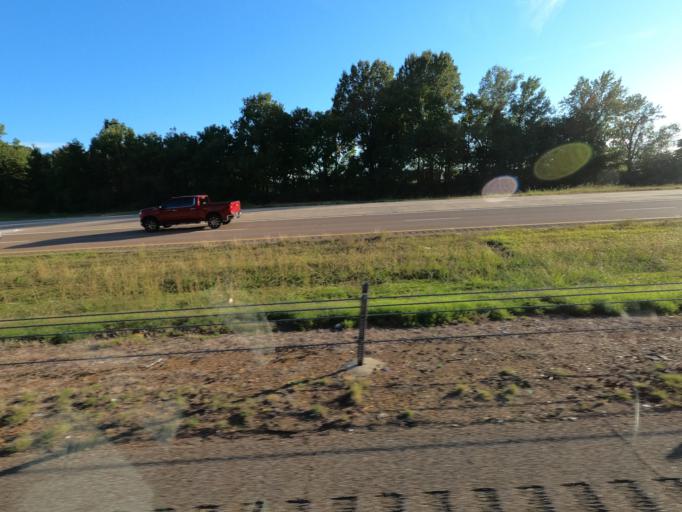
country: US
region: Tennessee
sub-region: Shelby County
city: Millington
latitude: 35.3081
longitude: -89.8285
